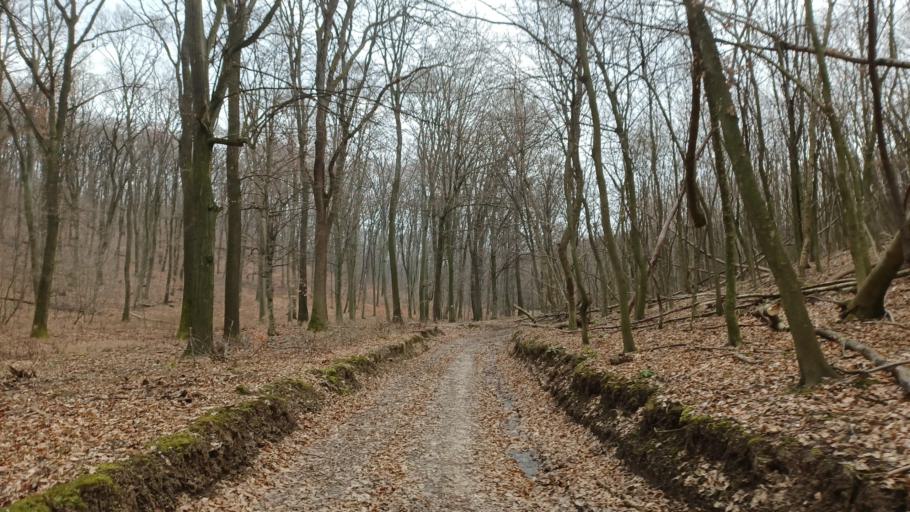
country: HU
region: Tolna
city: Szentgalpuszta
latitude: 46.3224
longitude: 18.6481
